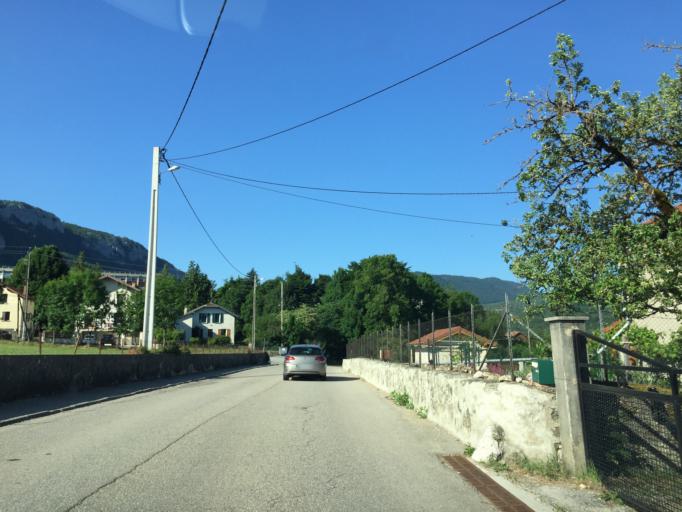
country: FR
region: Rhone-Alpes
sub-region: Departement de la Drome
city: Saint-Laurent-en-Royans
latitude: 44.9658
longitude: 5.4146
